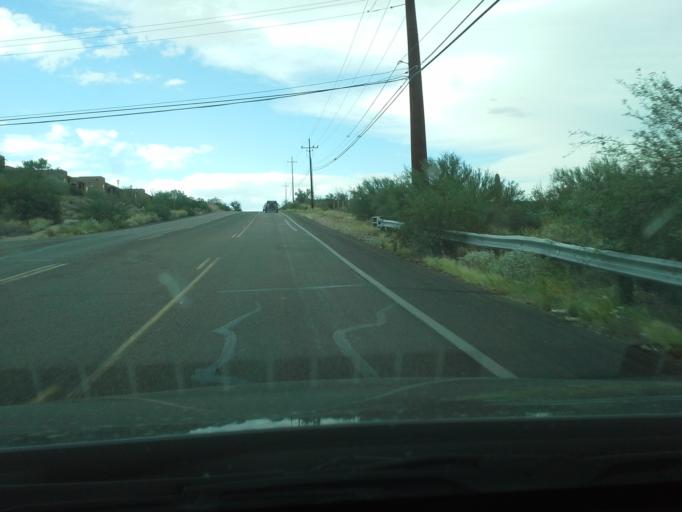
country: US
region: Arizona
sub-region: Pima County
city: South Tucson
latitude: 32.2212
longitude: -111.0202
